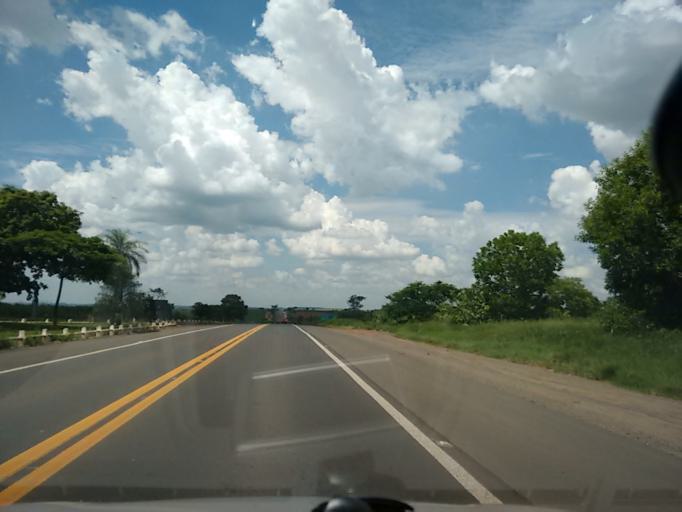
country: BR
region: Sao Paulo
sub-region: Osvaldo Cruz
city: Osvaldo Cruz
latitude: -21.9171
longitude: -50.8971
